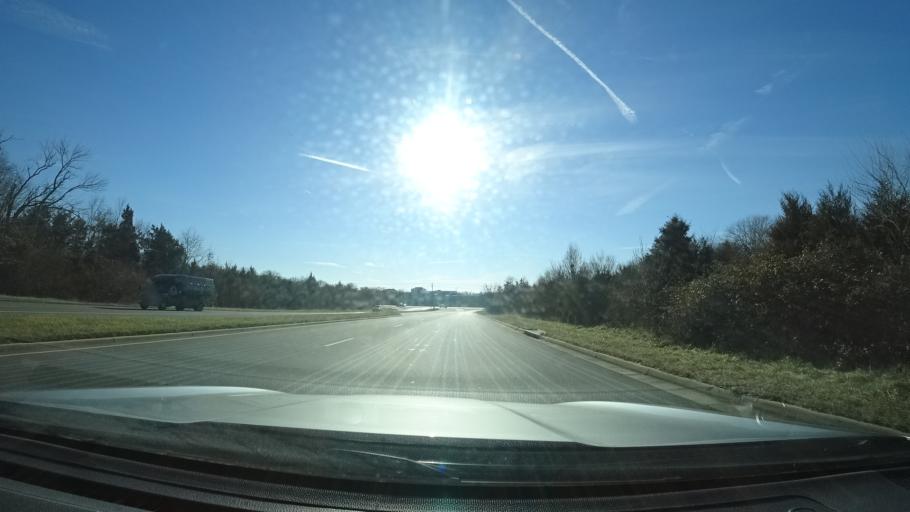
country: US
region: Virginia
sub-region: Fairfax County
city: Floris
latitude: 38.9461
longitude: -77.4219
